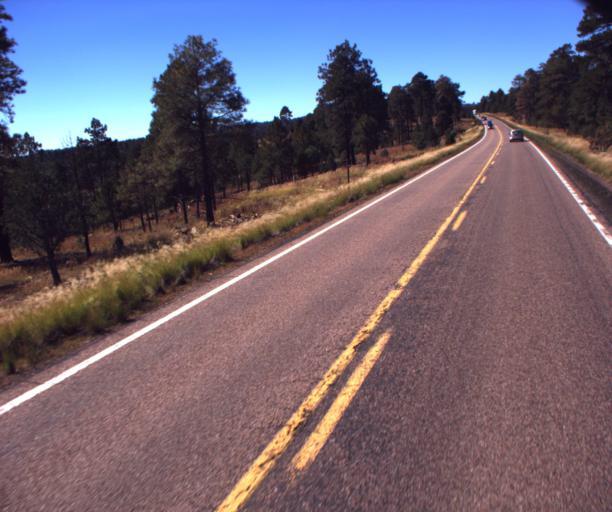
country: US
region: Arizona
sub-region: Navajo County
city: Heber-Overgaard
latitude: 34.3444
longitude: -110.7128
